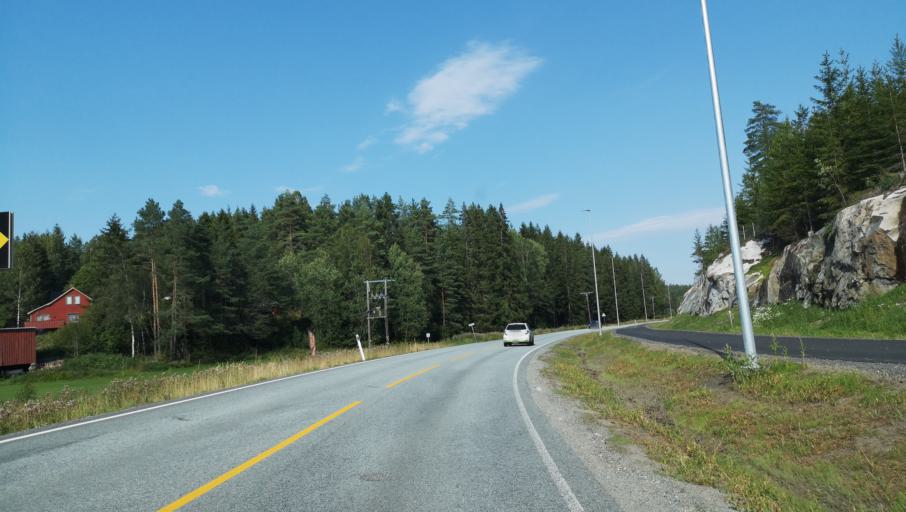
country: NO
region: Ostfold
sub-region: Valer
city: Kirkebygda
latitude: 59.4891
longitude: 10.8066
